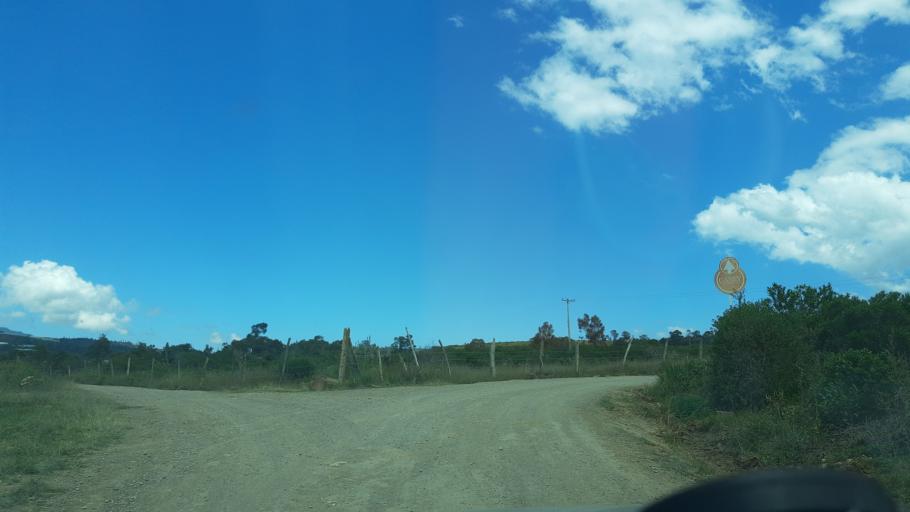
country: CO
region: Boyaca
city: Villa de Leiva
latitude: 5.6700
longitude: -73.5735
